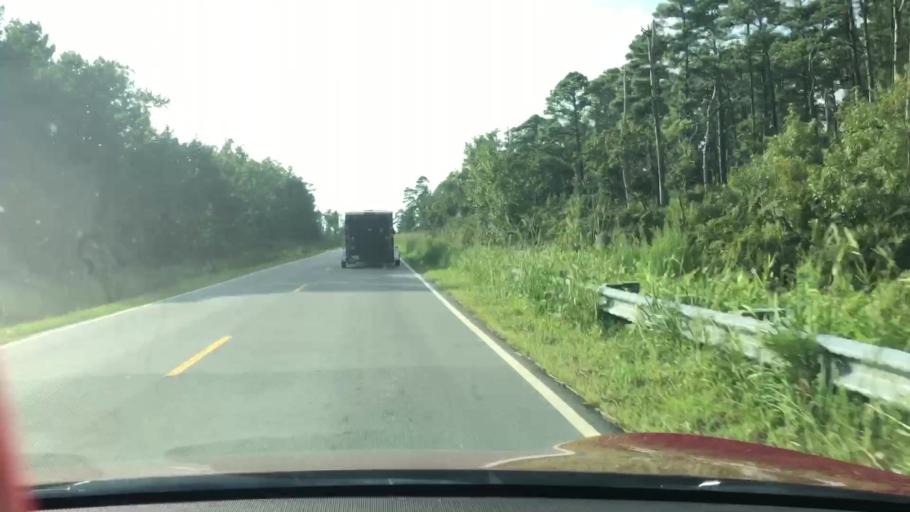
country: US
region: North Carolina
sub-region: Dare County
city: Wanchese
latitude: 35.6145
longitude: -75.8291
